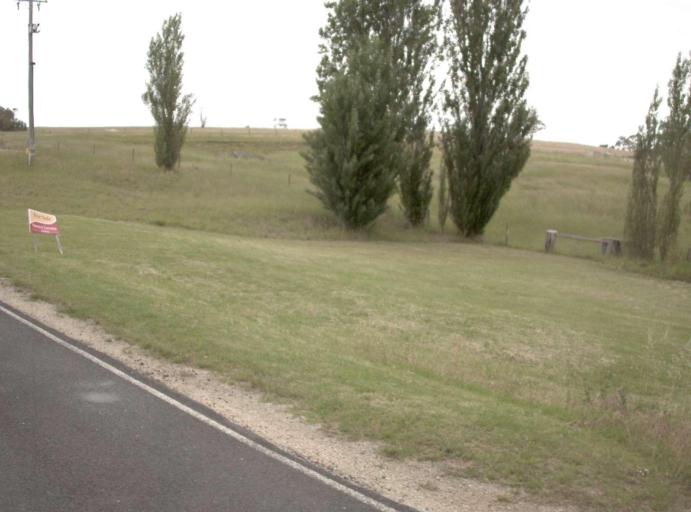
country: AU
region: Victoria
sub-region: Wellington
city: Sale
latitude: -38.1763
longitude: 147.1229
